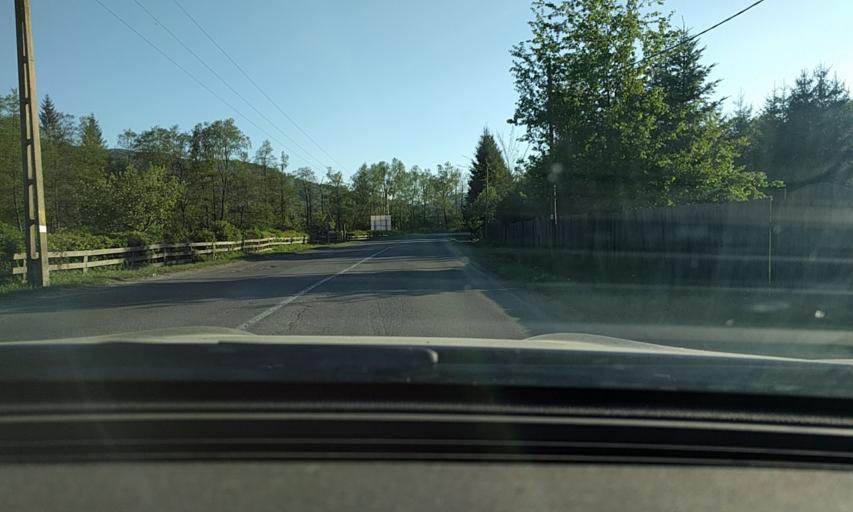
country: RO
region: Bacau
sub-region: Oras Slanic-Moldova
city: Cerdac
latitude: 46.1937
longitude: 26.5110
